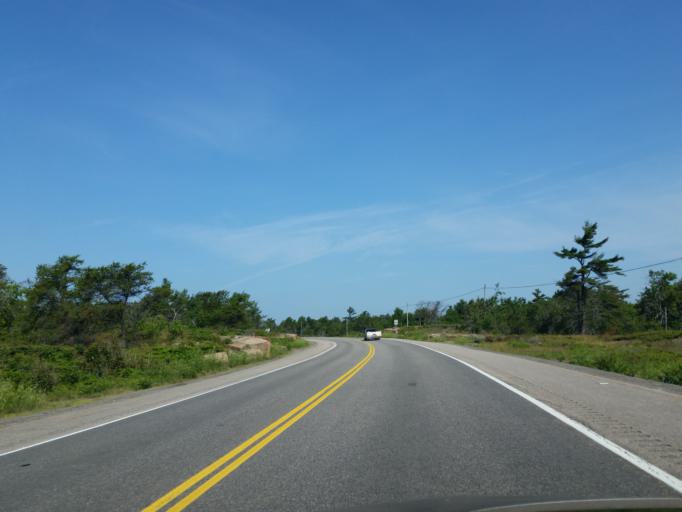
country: CA
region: Ontario
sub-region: Parry Sound District
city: Parry Sound
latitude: 45.7791
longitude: -80.5012
